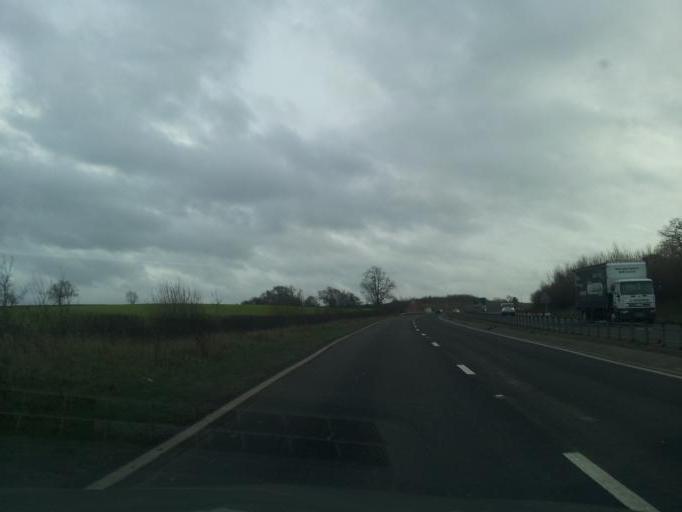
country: GB
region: England
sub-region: Central Bedfordshire
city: Leighton Buzzard
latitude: 51.9326
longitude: -0.6966
